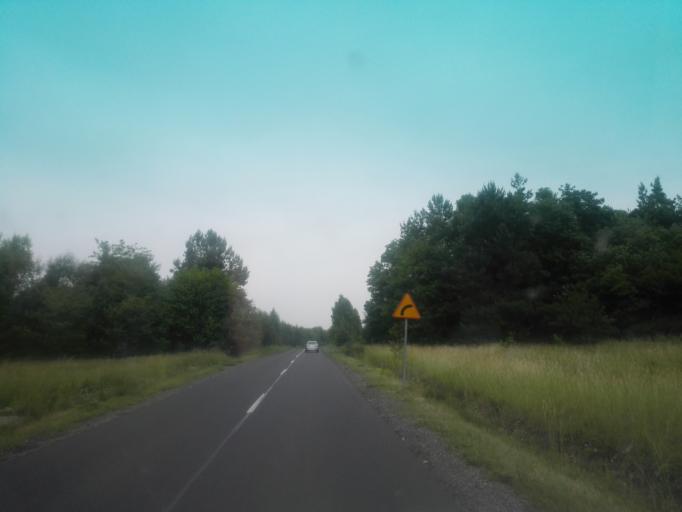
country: PL
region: Silesian Voivodeship
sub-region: Powiat czestochowski
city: Olsztyn
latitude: 50.7859
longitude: 19.2731
